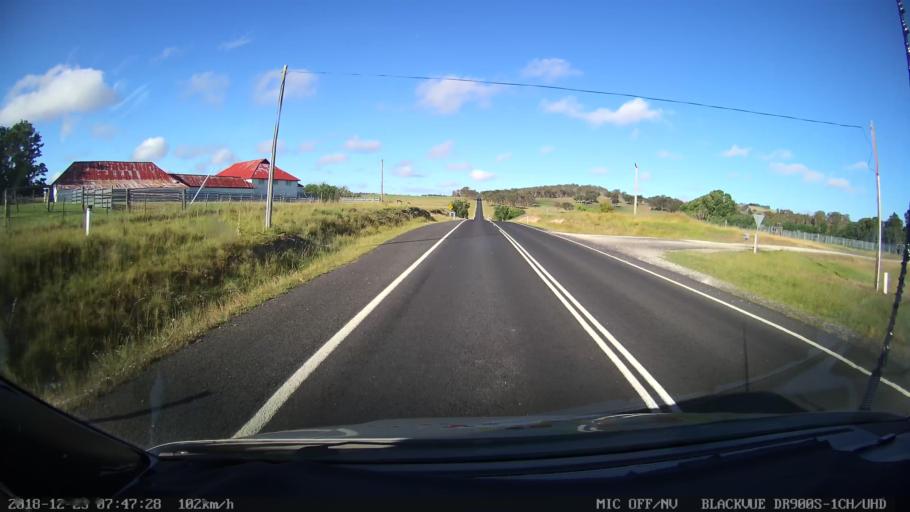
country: AU
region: New South Wales
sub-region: Armidale Dumaresq
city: Enmore
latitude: -30.5271
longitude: 151.9006
